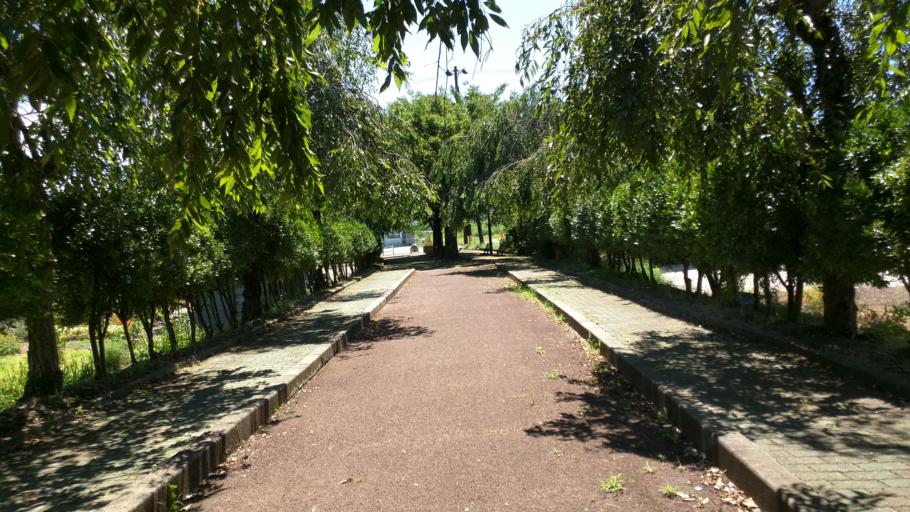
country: JP
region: Fukushima
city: Kitakata
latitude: 37.6453
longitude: 139.8630
